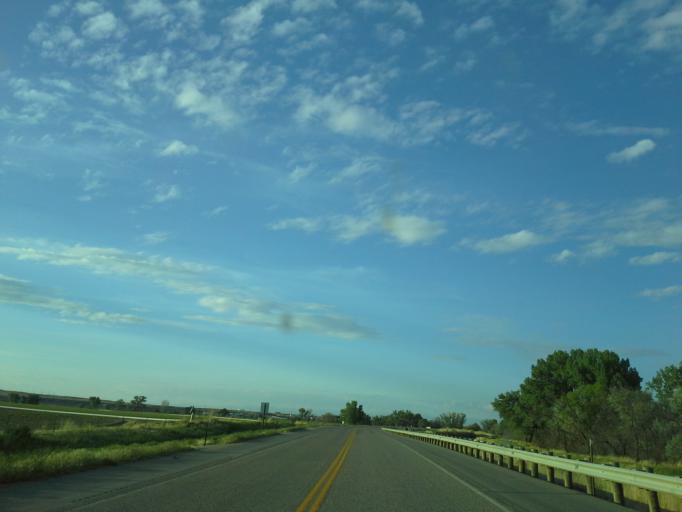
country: US
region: Wyoming
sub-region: Washakie County
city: Worland
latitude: 44.0011
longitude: -107.9876
